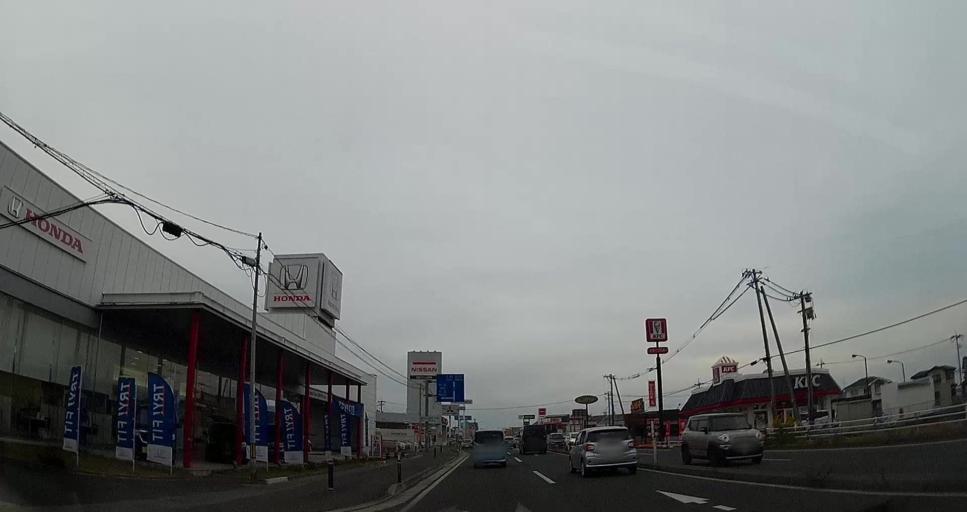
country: JP
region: Miyagi
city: Iwanuma
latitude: 38.1778
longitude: 140.8905
